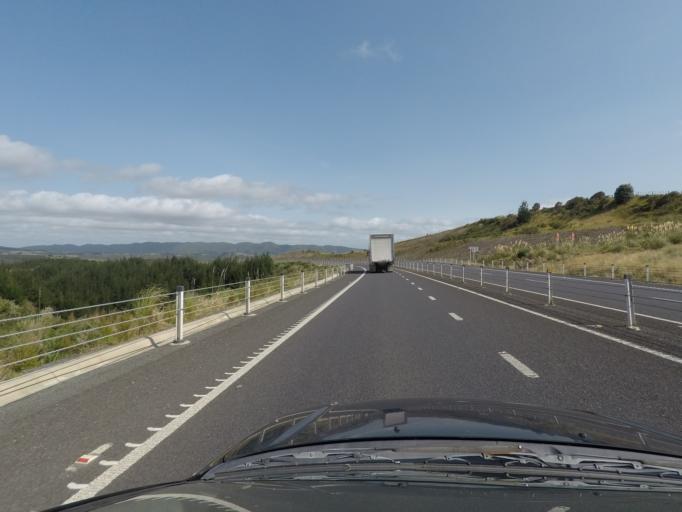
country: NZ
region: Northland
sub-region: Whangarei
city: Ruakaka
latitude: -36.0548
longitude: 174.4252
